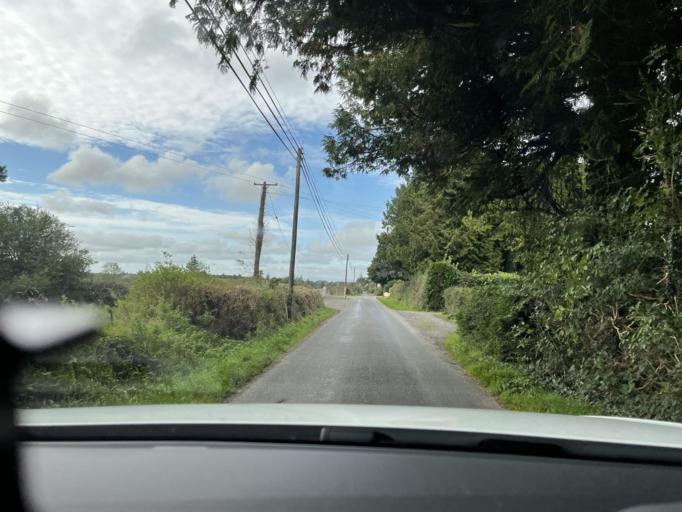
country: IE
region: Connaught
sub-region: Roscommon
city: Boyle
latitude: 54.0199
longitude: -8.3800
